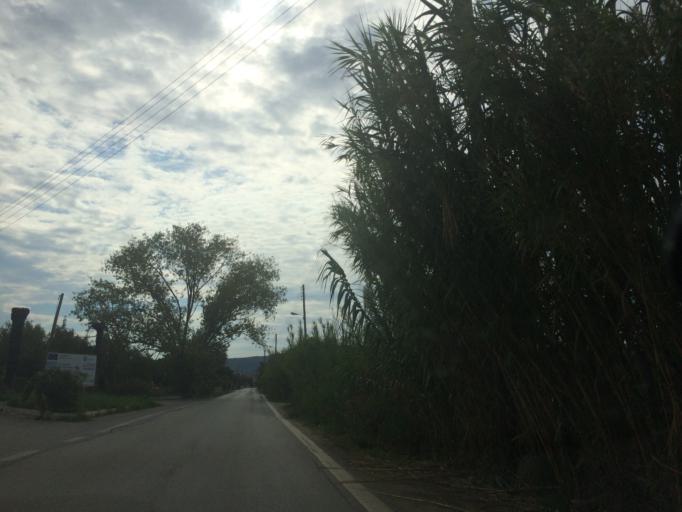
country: GR
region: Peloponnese
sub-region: Nomos Messinias
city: Pylos
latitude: 36.9489
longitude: 21.7048
